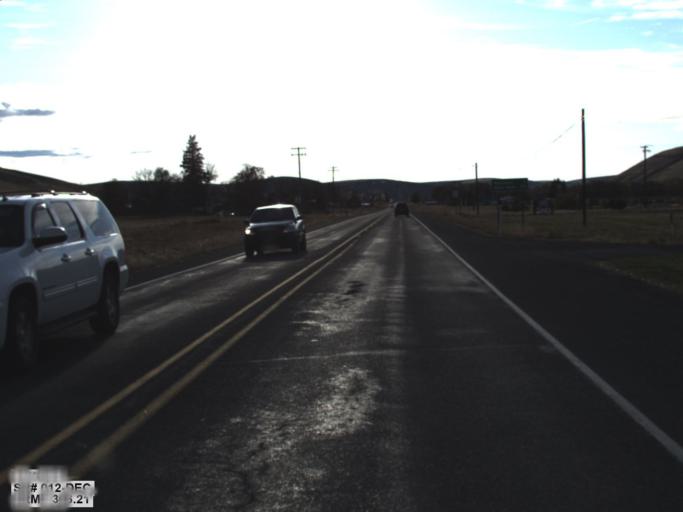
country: US
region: Washington
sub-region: Columbia County
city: Dayton
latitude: 46.3107
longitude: -117.9946
